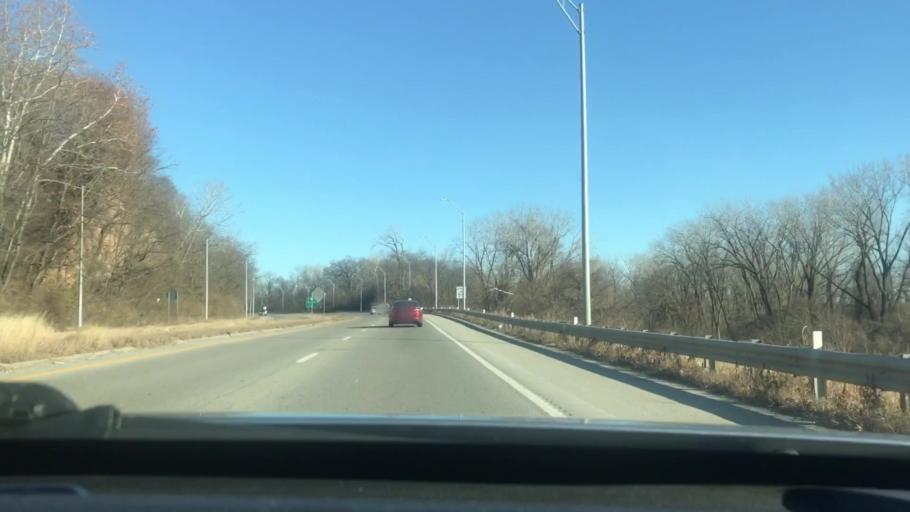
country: US
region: Missouri
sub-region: Clay County
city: North Kansas City
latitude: 39.1472
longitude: -94.5450
